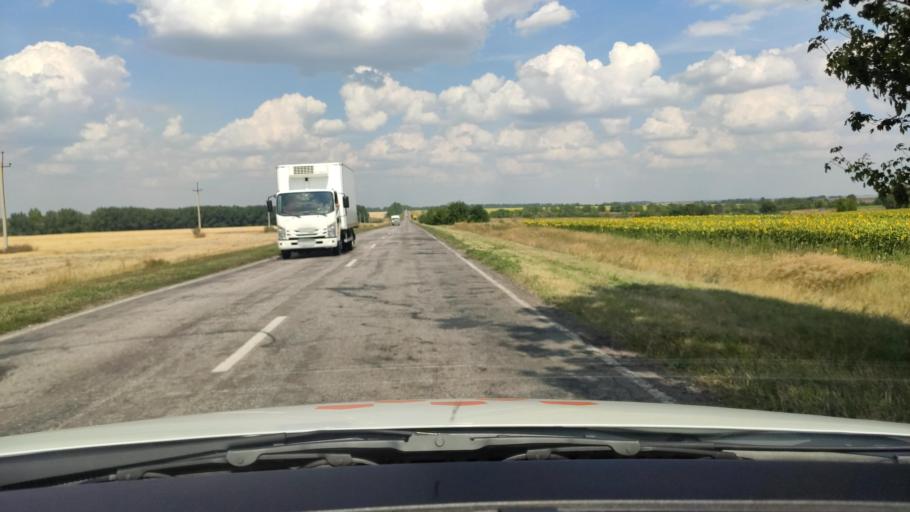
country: RU
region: Voronezj
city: Pereleshinskiy
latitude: 51.7414
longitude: 40.3985
